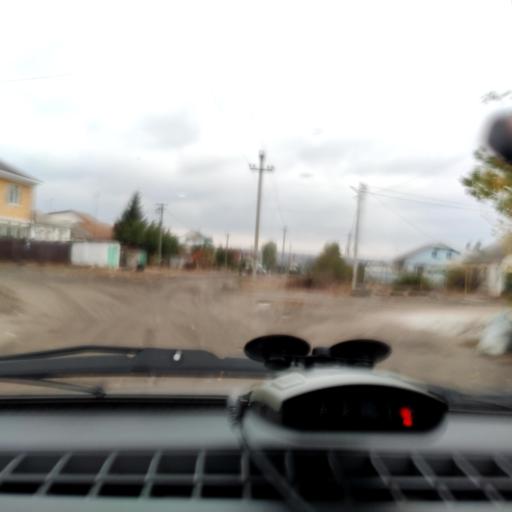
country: RU
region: Voronezj
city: Pridonskoy
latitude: 51.7024
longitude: 39.0708
